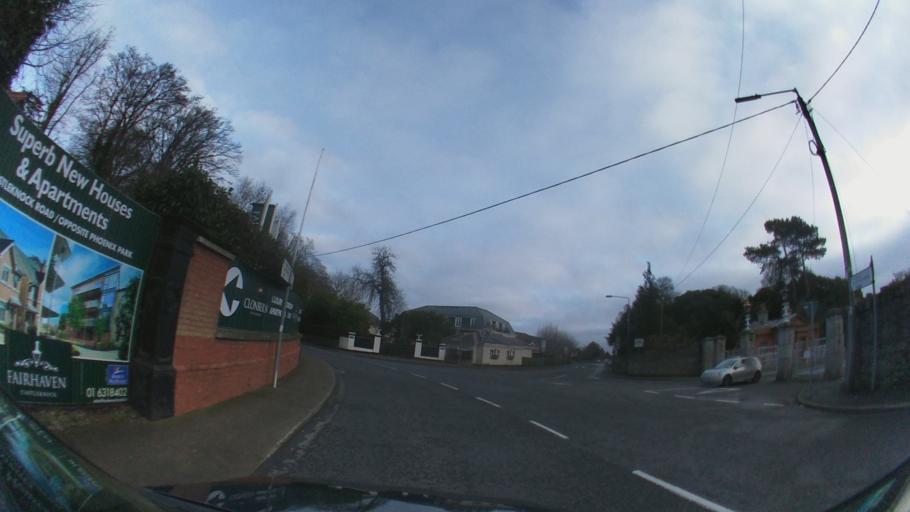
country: IE
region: Leinster
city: Chapelizod
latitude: 53.3709
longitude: -6.3340
